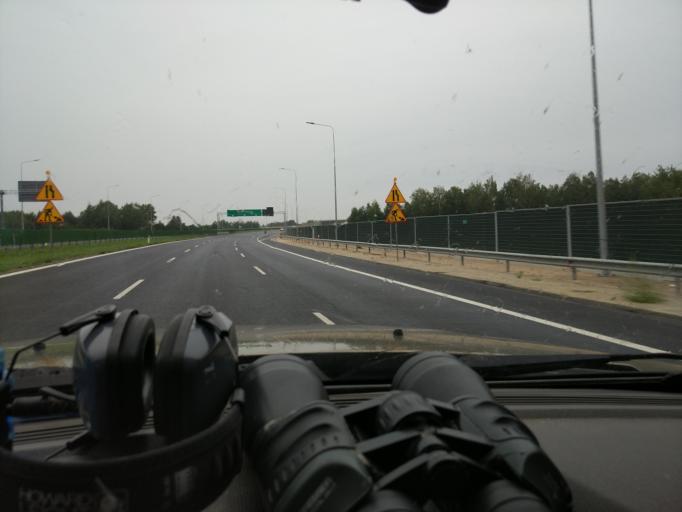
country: PL
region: Masovian Voivodeship
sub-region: Powiat wolominski
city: Slupno
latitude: 52.3494
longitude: 21.1591
